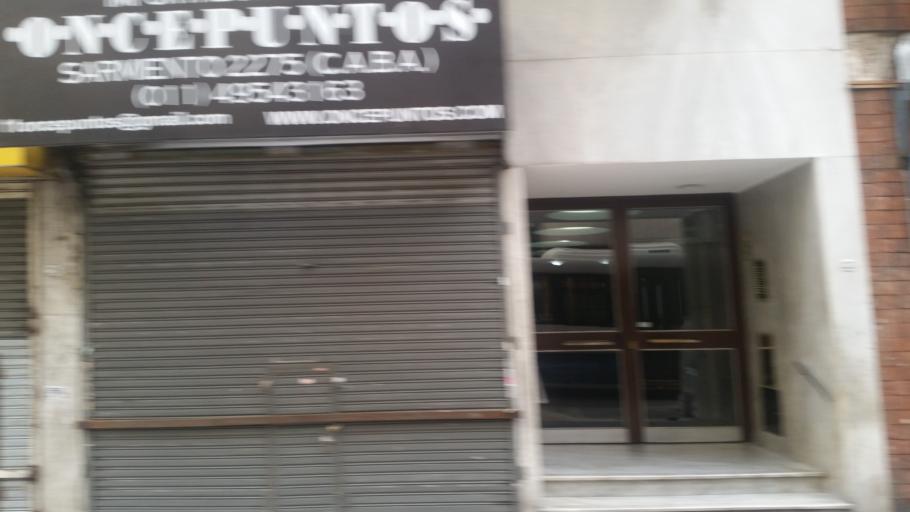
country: AR
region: Buenos Aires F.D.
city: Buenos Aires
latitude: -34.6061
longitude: -58.3988
